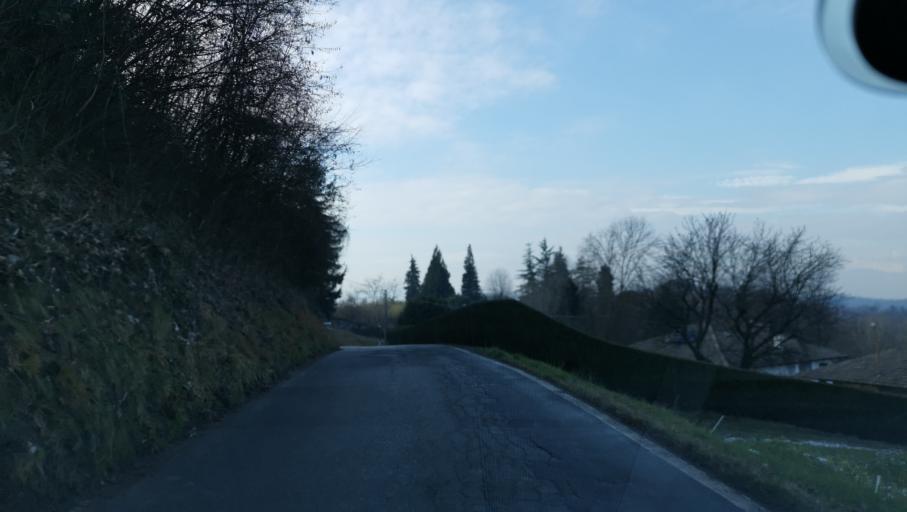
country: IT
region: Piedmont
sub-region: Provincia di Torino
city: Sciolze
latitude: 45.0968
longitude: 7.8661
